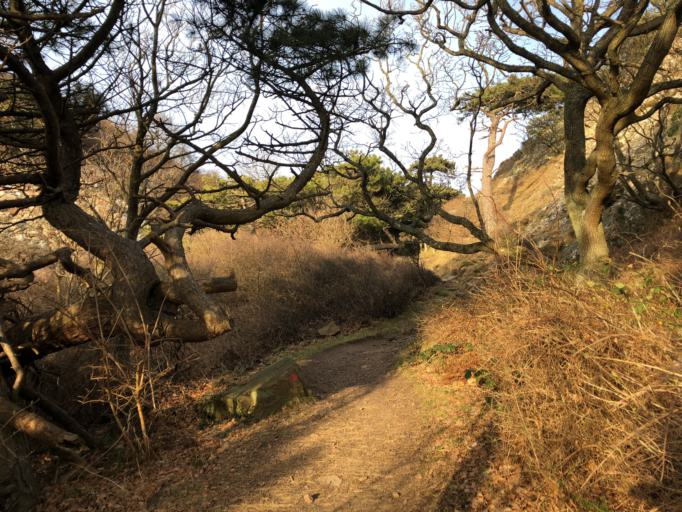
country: SE
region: Skane
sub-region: Hoganas Kommun
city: Hoganas
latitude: 56.2997
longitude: 12.4525
